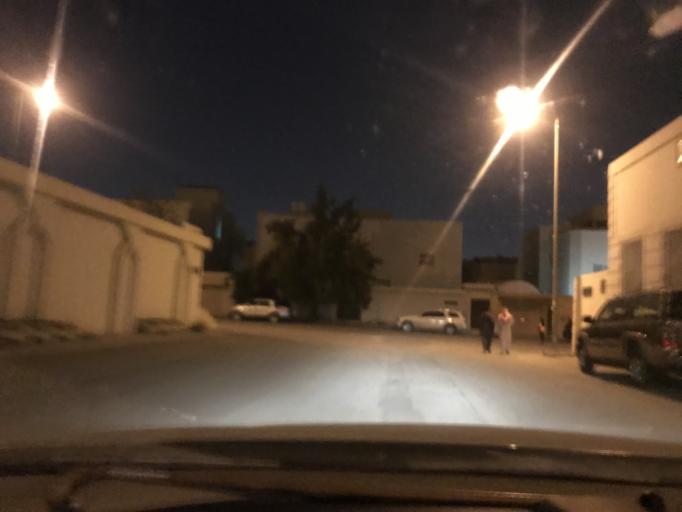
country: SA
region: Ar Riyad
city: Riyadh
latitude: 24.7556
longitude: 46.7531
